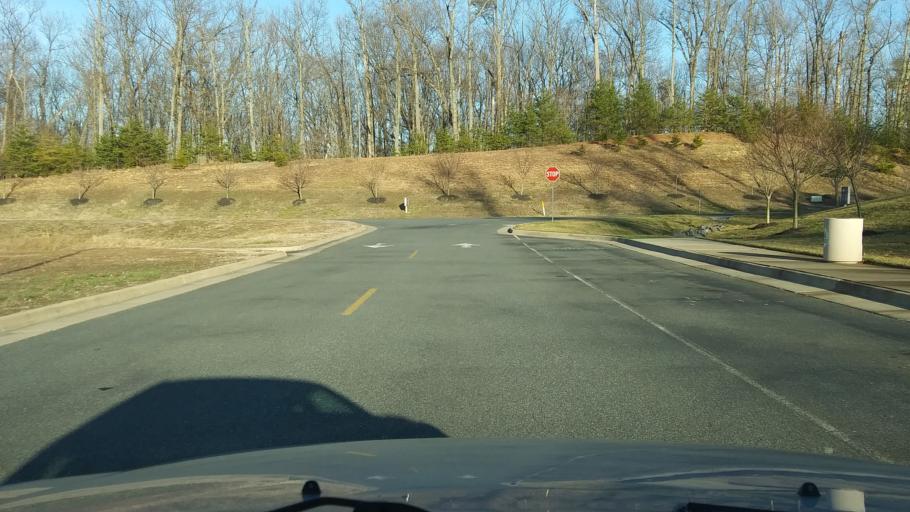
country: US
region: Virginia
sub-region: Prince William County
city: Triangle
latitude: 38.5444
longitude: -77.3405
